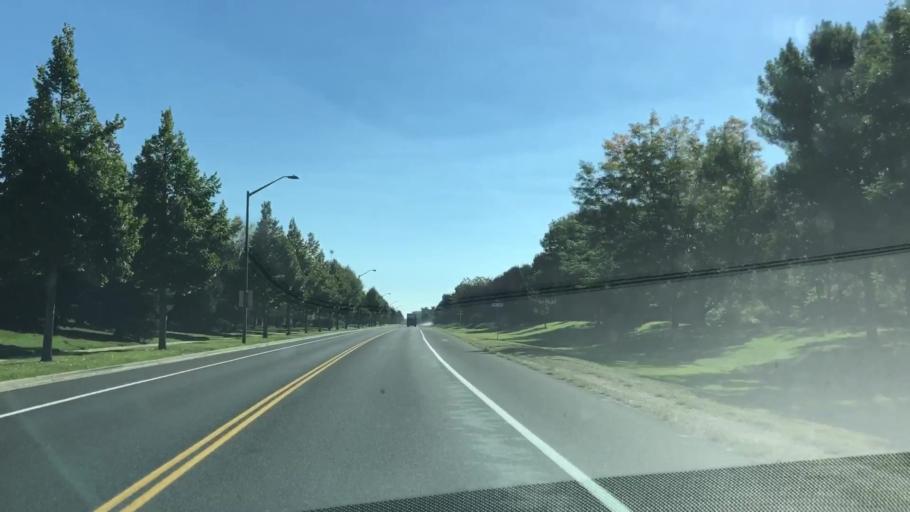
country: US
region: Colorado
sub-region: Larimer County
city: Fort Collins
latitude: 40.5092
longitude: -105.0286
